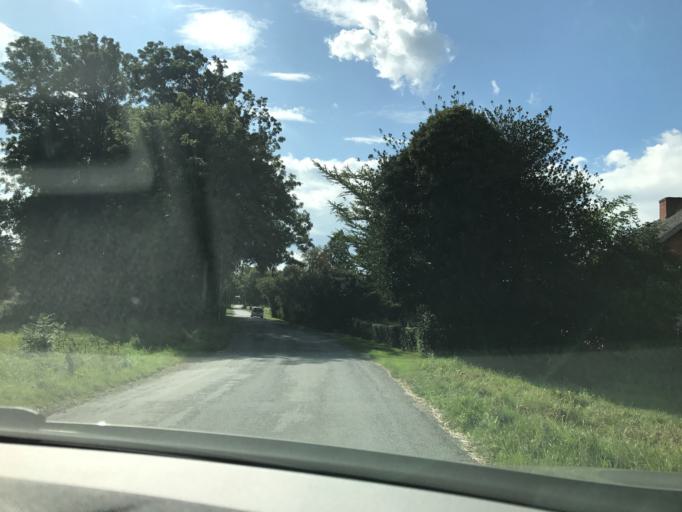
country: DK
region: South Denmark
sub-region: Middelfart Kommune
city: Norre Aby
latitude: 55.4435
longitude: 9.8250
